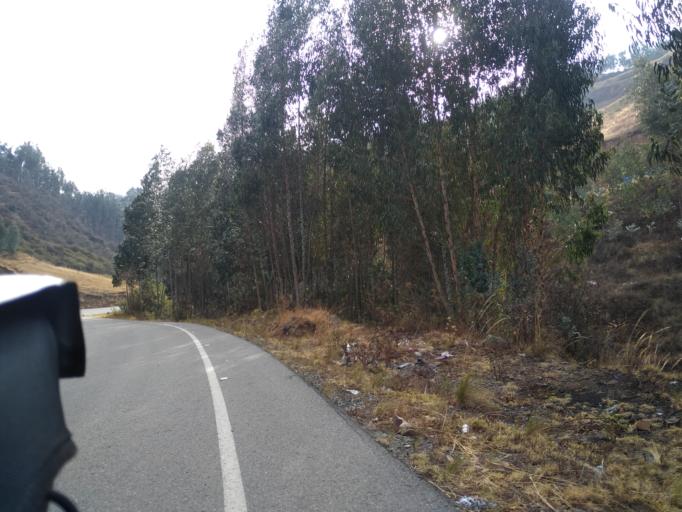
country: PE
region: La Libertad
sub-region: Provincia de Otuzco
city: Agallpampa
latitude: -7.9902
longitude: -78.5343
